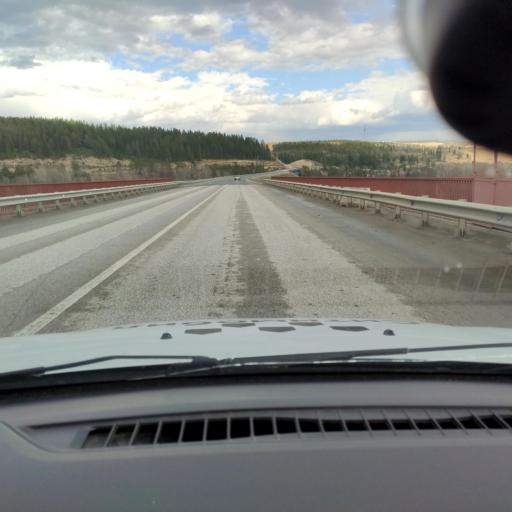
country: RU
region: Perm
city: Chusovoy
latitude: 58.3303
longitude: 57.7721
